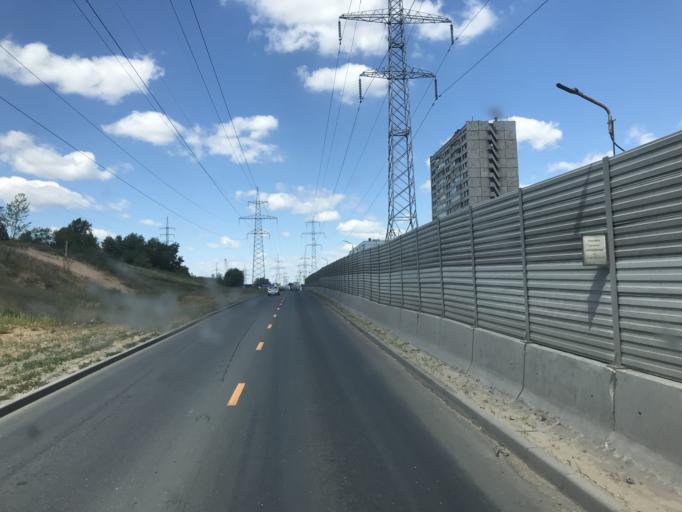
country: RU
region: Samara
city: Zhigulevsk
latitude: 53.4728
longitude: 49.5121
